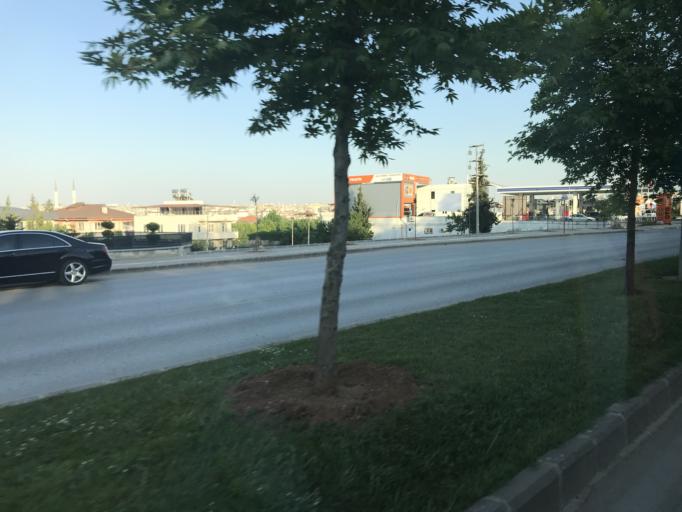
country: TR
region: Gaziantep
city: Sahinbey
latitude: 37.0560
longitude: 37.3208
